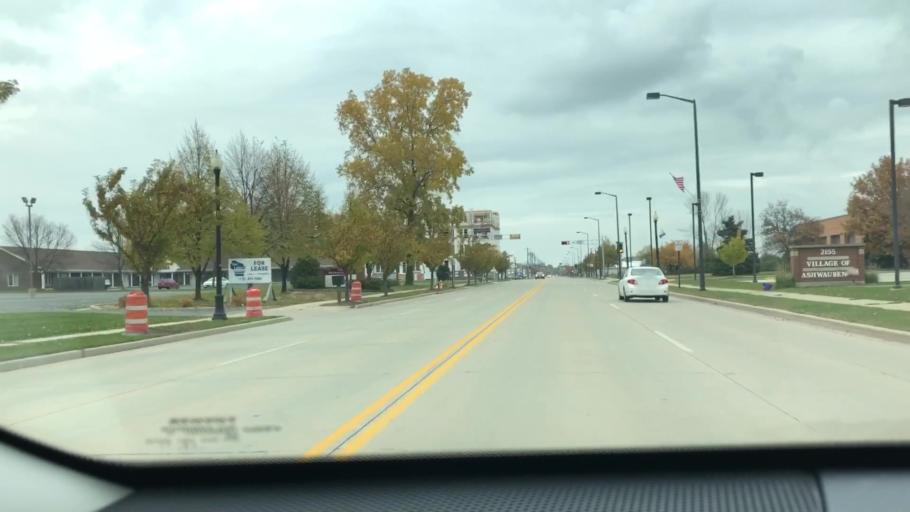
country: US
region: Wisconsin
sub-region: Brown County
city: Ashwaubenon
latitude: 44.4913
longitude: -88.0579
